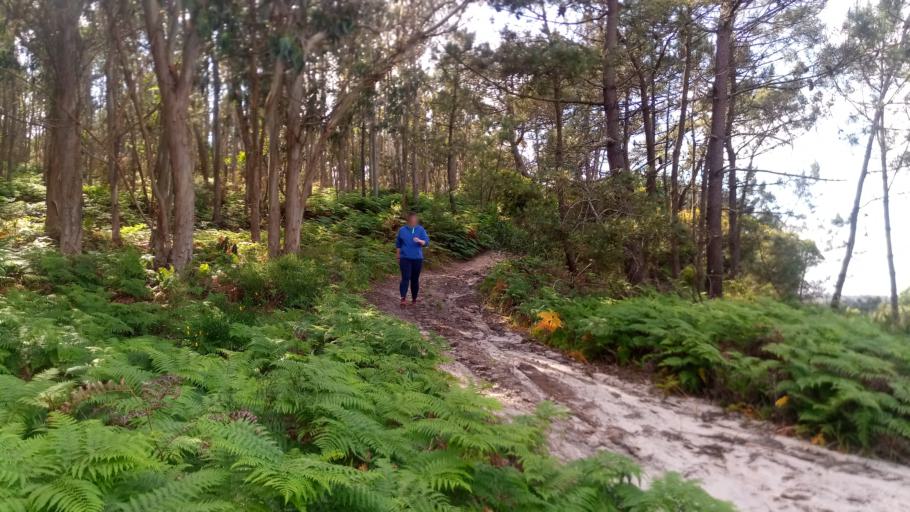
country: PT
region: Leiria
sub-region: Obidos
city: Obidos
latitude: 39.3934
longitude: -9.2116
